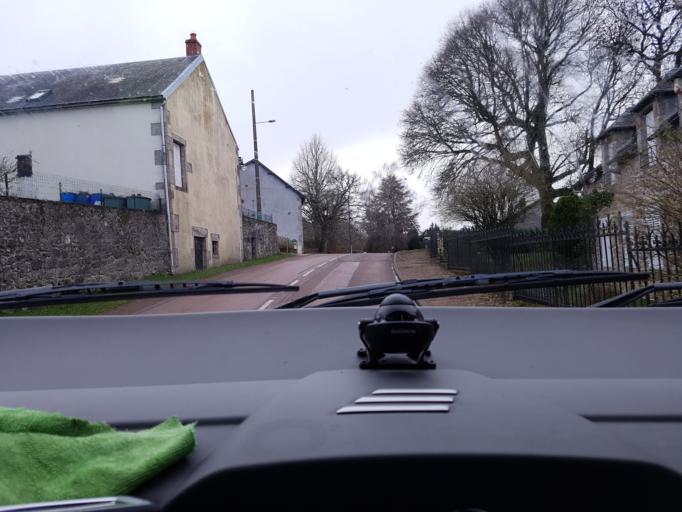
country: FR
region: Bourgogne
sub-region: Departement de la Cote-d'Or
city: Saulieu
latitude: 47.2707
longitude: 4.0294
